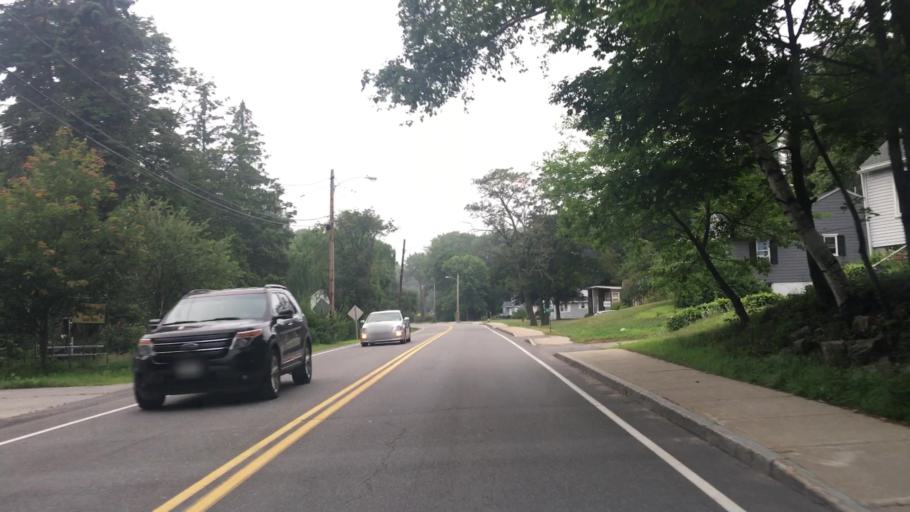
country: US
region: Maine
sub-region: York County
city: Kittery
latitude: 43.0924
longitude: -70.7370
